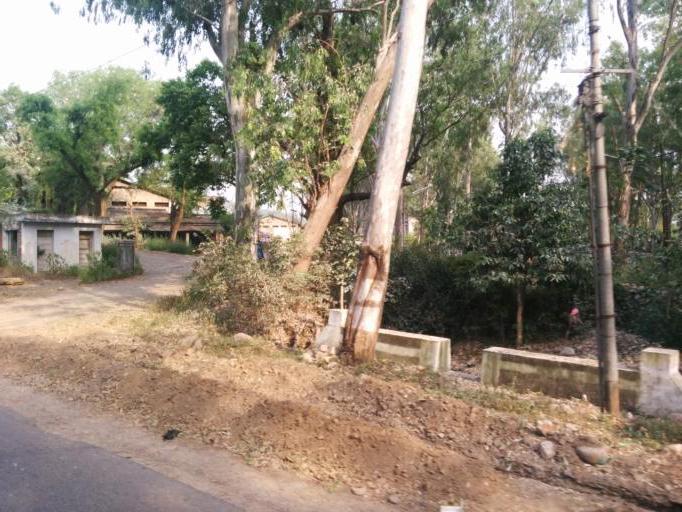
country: IN
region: Punjab
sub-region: Gurdaspur
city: Dharkalan
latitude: 32.2836
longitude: 75.8570
